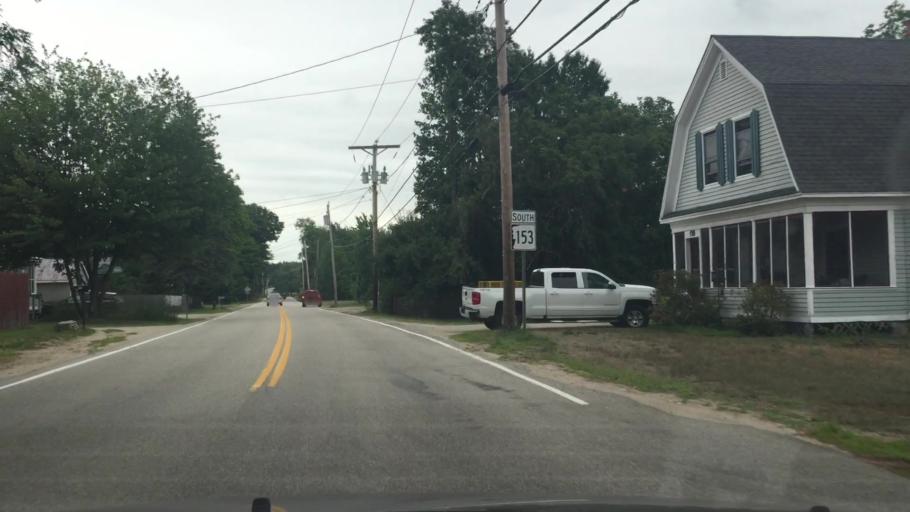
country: US
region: New Hampshire
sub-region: Carroll County
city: Conway
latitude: 43.9738
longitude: -71.1166
